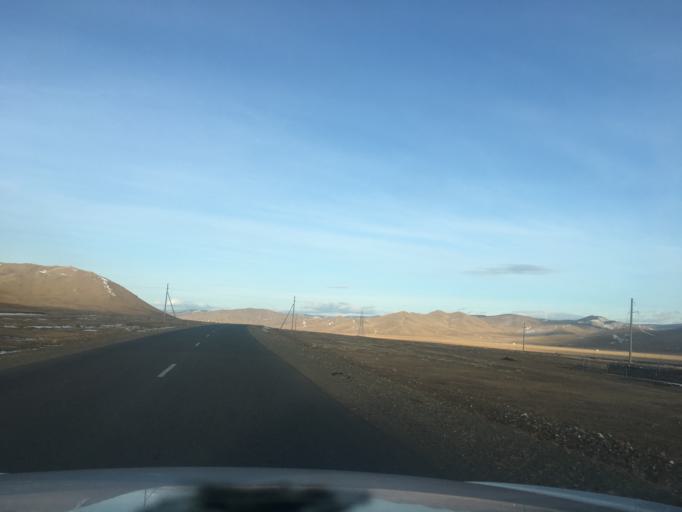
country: MN
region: Central Aimak
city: Mandal
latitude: 48.1070
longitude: 106.6302
